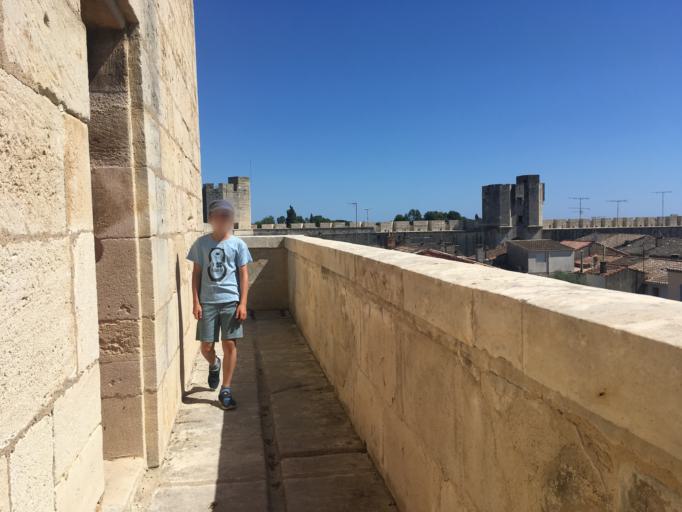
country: FR
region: Languedoc-Roussillon
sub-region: Departement du Gard
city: Aigues-Mortes
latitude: 43.5663
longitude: 4.1943
